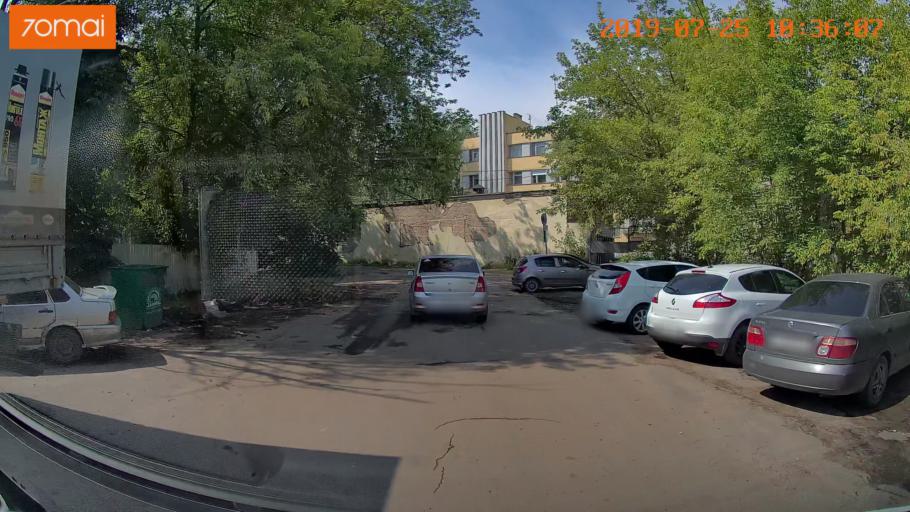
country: RU
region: Ivanovo
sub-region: Gorod Ivanovo
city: Ivanovo
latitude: 57.0114
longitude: 40.9961
